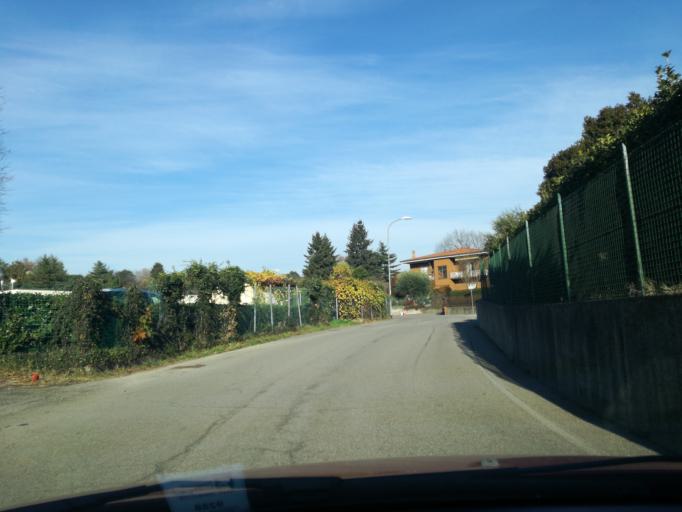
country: IT
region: Lombardy
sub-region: Provincia di Lecco
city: Merate
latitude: 45.6978
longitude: 9.4290
